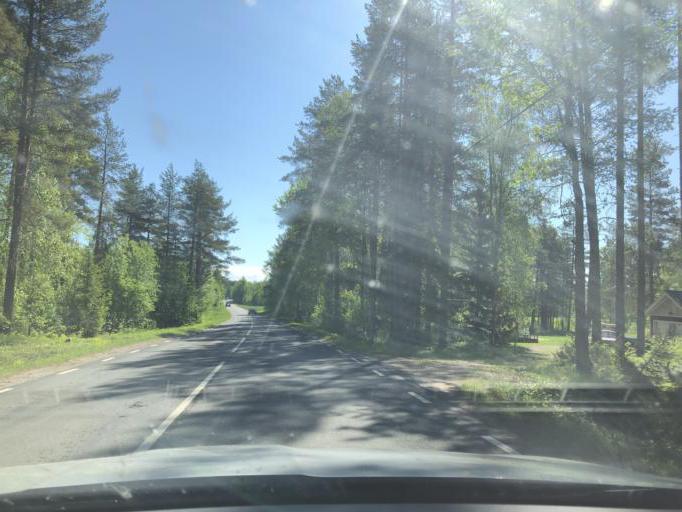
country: SE
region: Norrbotten
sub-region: Lulea Kommun
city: Sodra Sunderbyn
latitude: 65.6613
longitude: 21.9790
